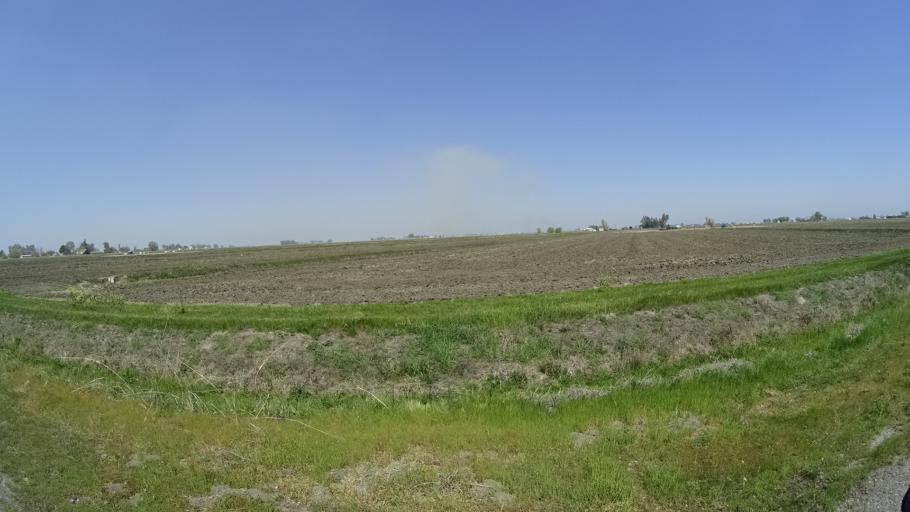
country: US
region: California
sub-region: Glenn County
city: Willows
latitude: 39.5515
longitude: -122.0951
